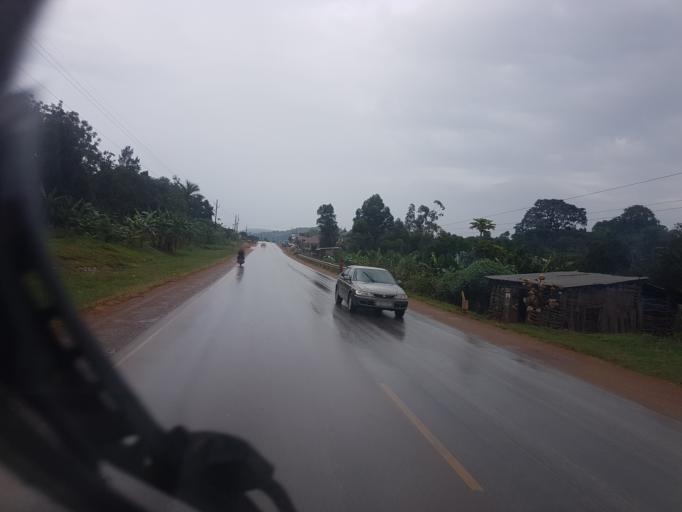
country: UG
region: Central Region
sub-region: Mpigi District
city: Mpigi
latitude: 0.1946
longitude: 32.2967
